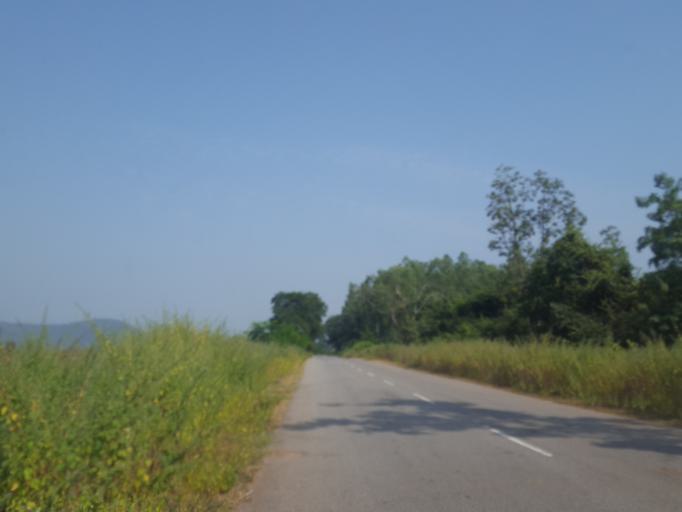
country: IN
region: Telangana
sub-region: Khammam
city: Yellandu
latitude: 17.6665
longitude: 80.2743
